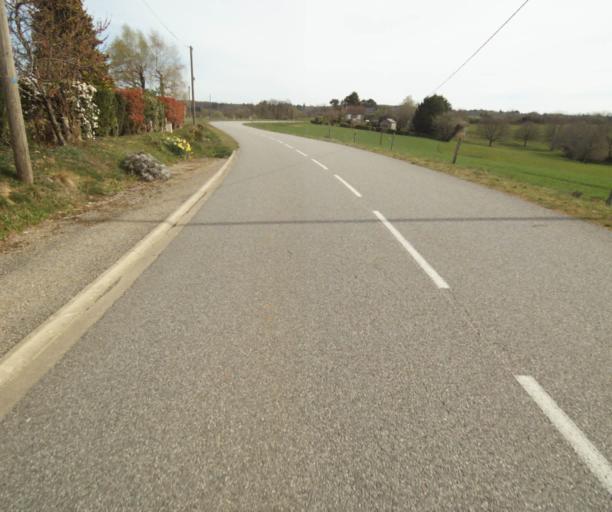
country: FR
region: Limousin
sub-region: Departement de la Correze
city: Correze
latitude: 45.3888
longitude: 1.8129
